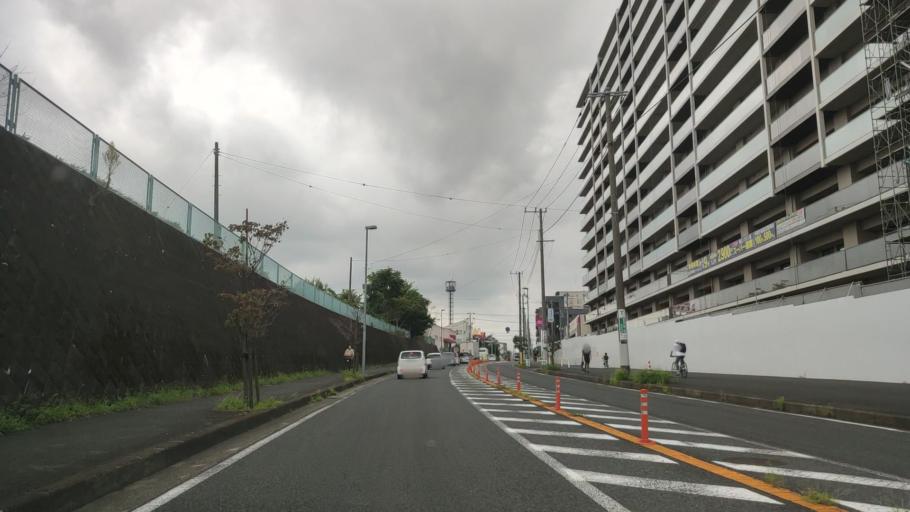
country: JP
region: Kanagawa
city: Minami-rinkan
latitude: 35.5024
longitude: 139.4587
